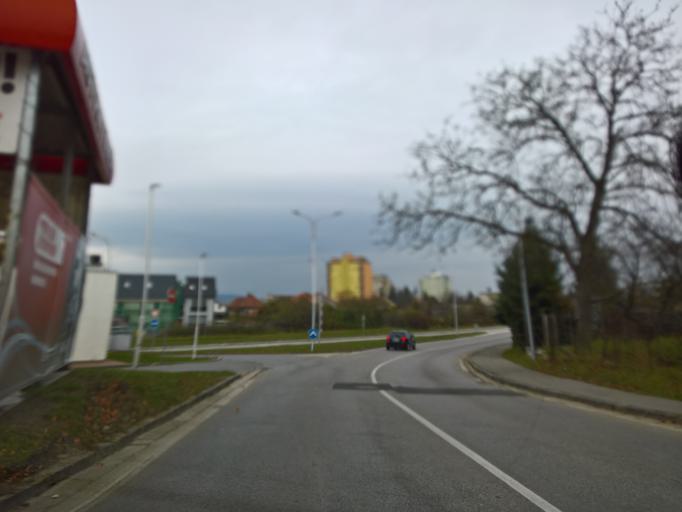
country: SK
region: Nitriansky
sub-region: Okres Nitra
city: Nitra
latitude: 48.3069
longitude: 18.0733
